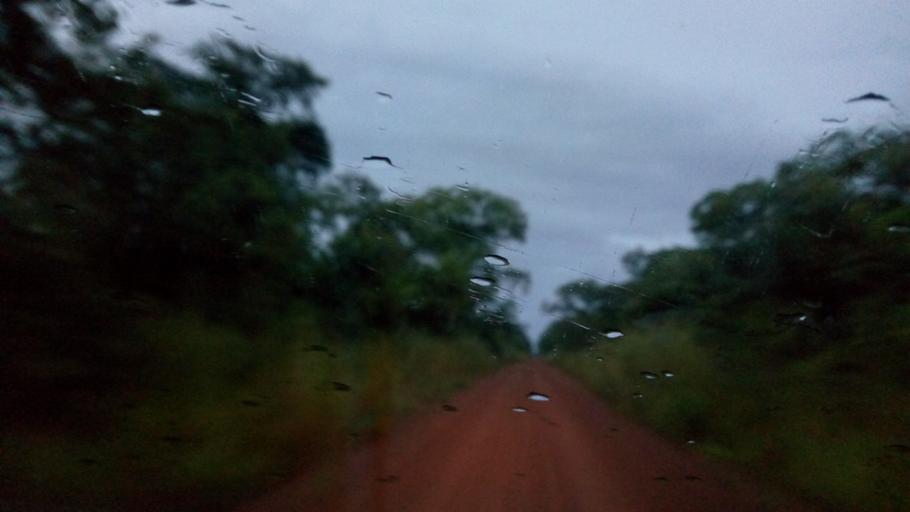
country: ZM
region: Luapula
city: Nchelenge
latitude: -9.8283
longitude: 28.1326
